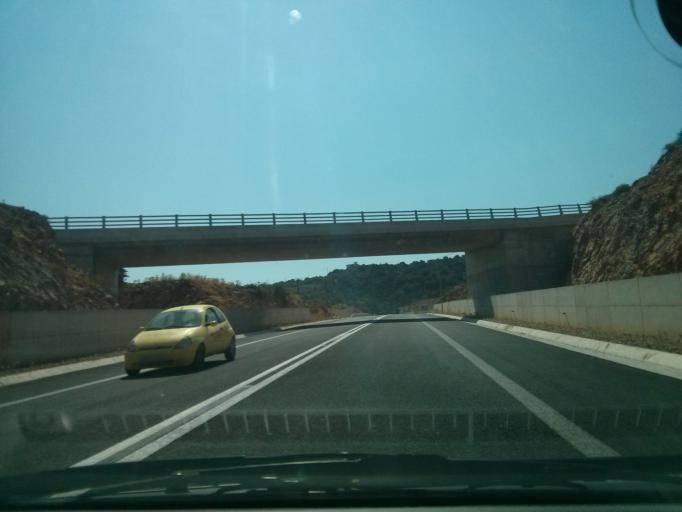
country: GR
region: Crete
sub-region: Nomos Lasithiou
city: Agios Nikolaos
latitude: 35.1645
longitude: 25.7044
